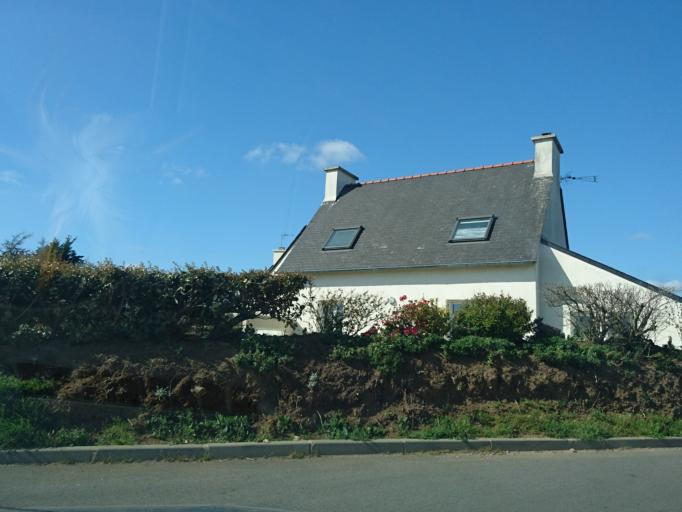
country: FR
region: Brittany
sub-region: Departement du Finistere
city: Lanrivoare
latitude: 48.4678
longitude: -4.6412
